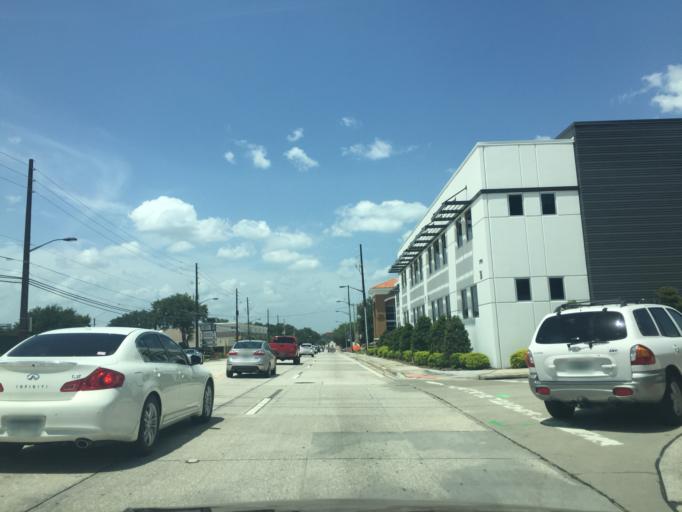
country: US
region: Florida
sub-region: Orange County
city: Orlando
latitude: 28.5666
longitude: -81.3644
